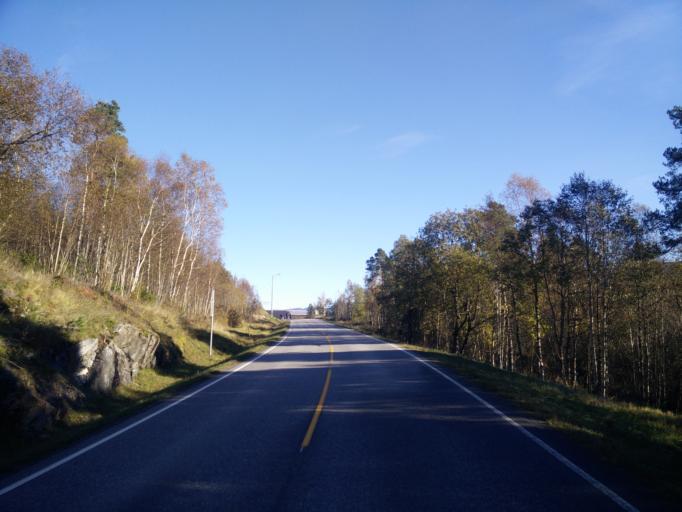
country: NO
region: More og Romsdal
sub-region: Tingvoll
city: Tingvoll
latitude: 63.0350
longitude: 8.0365
